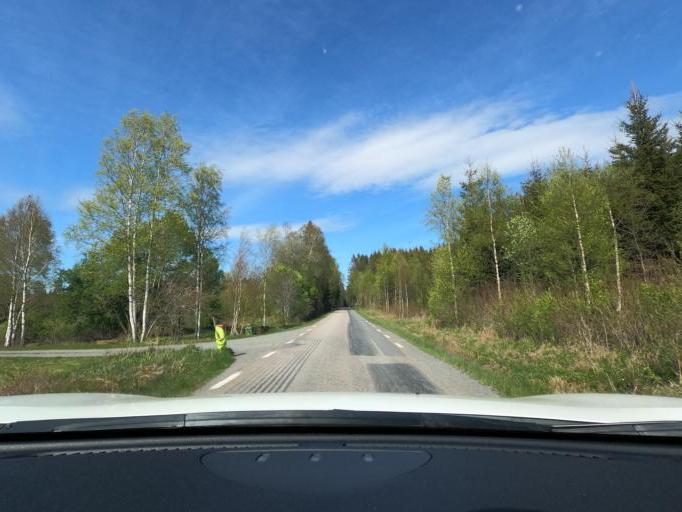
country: SE
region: Vaestra Goetaland
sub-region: Marks Kommun
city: Horred
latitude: 57.4424
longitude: 12.4315
